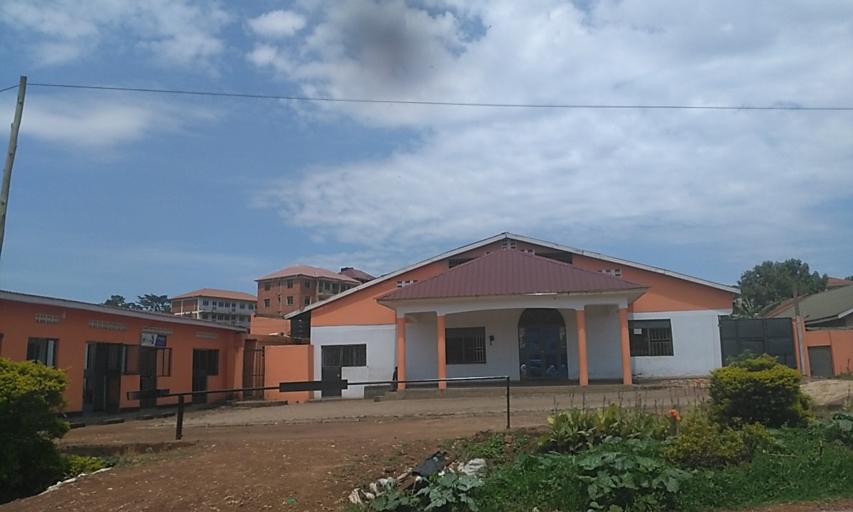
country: UG
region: Central Region
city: Kampala Central Division
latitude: 0.3516
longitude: 32.5775
